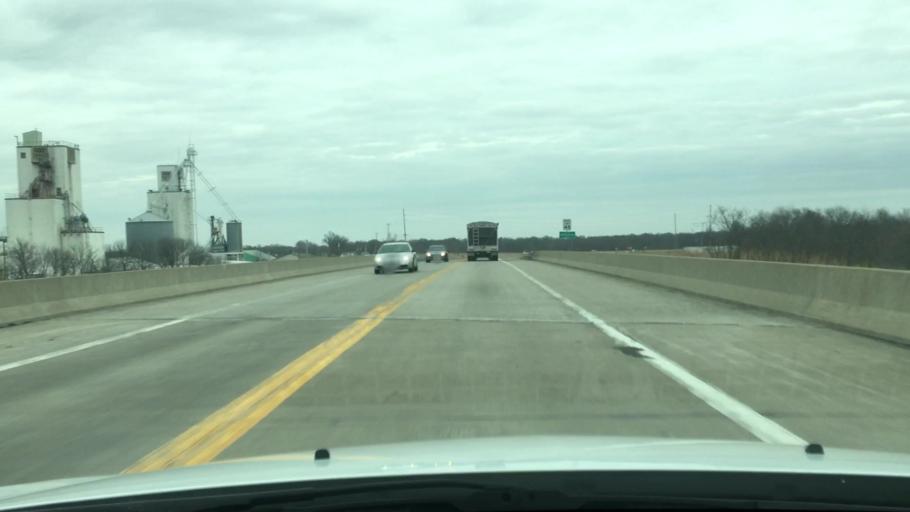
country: US
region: Missouri
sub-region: Audrain County
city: Mexico
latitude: 39.1568
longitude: -91.8430
